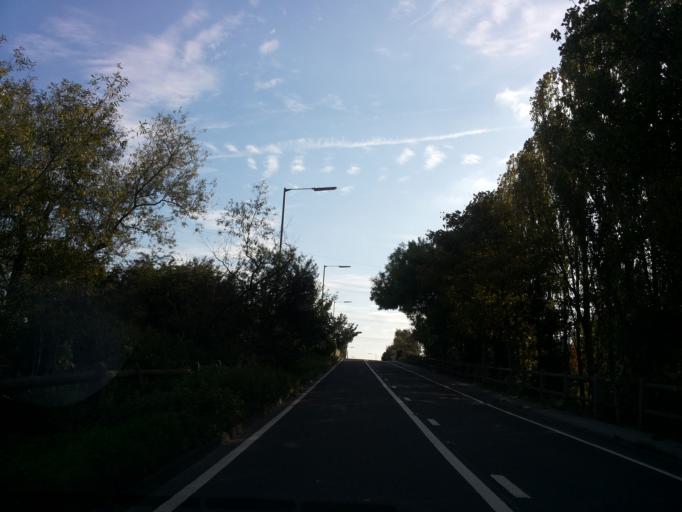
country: GB
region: England
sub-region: North Yorkshire
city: Camblesforth
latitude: 53.7192
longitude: -1.0187
